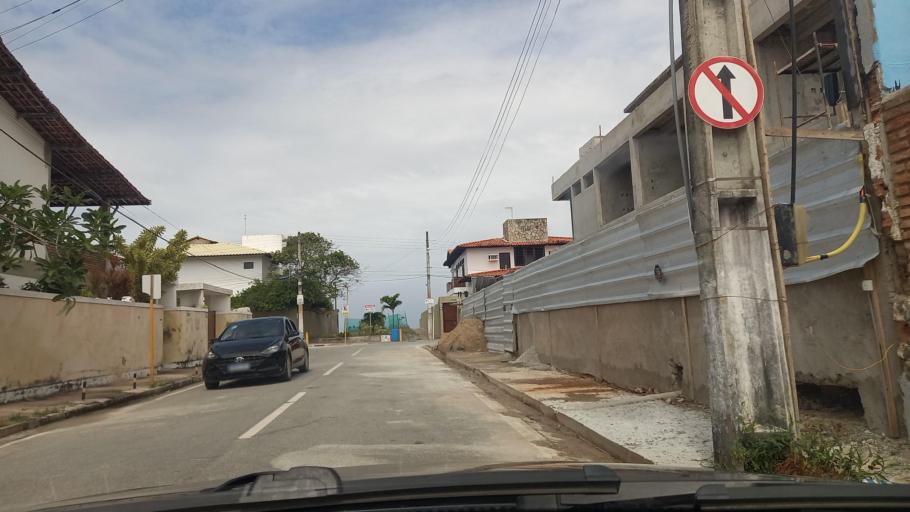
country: BR
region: Alagoas
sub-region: Marechal Deodoro
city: Marechal Deodoro
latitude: -9.8410
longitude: -35.8929
